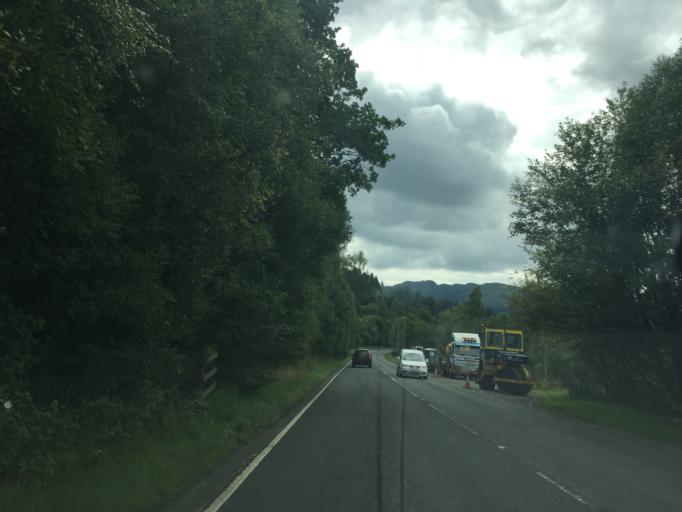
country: GB
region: Scotland
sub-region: Stirling
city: Callander
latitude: 56.3361
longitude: -4.3246
